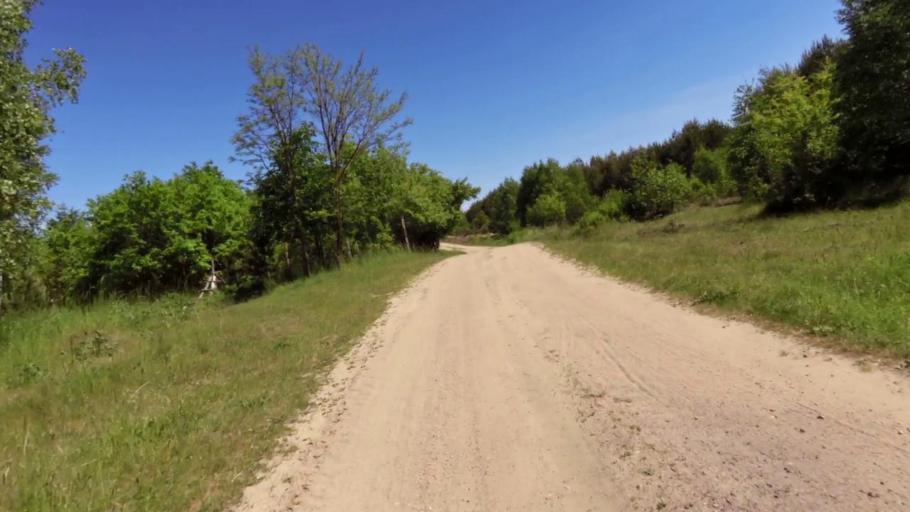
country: PL
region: West Pomeranian Voivodeship
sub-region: Powiat szczecinecki
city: Borne Sulinowo
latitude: 53.5839
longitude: 16.6504
